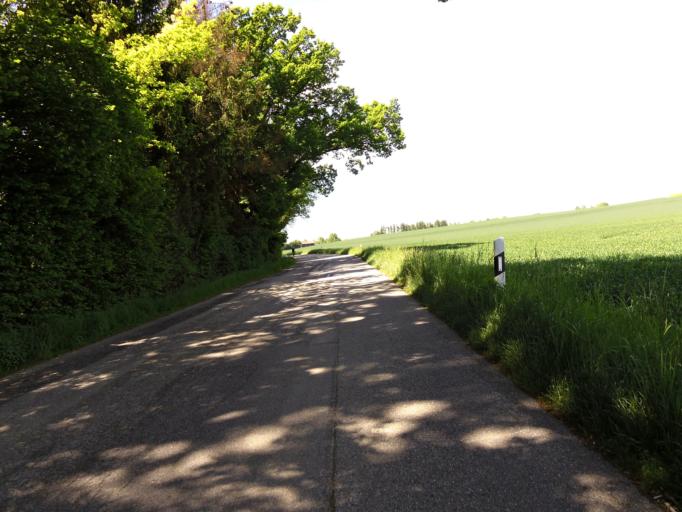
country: DE
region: Bavaria
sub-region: Upper Bavaria
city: Moosburg
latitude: 48.4772
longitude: 11.9084
